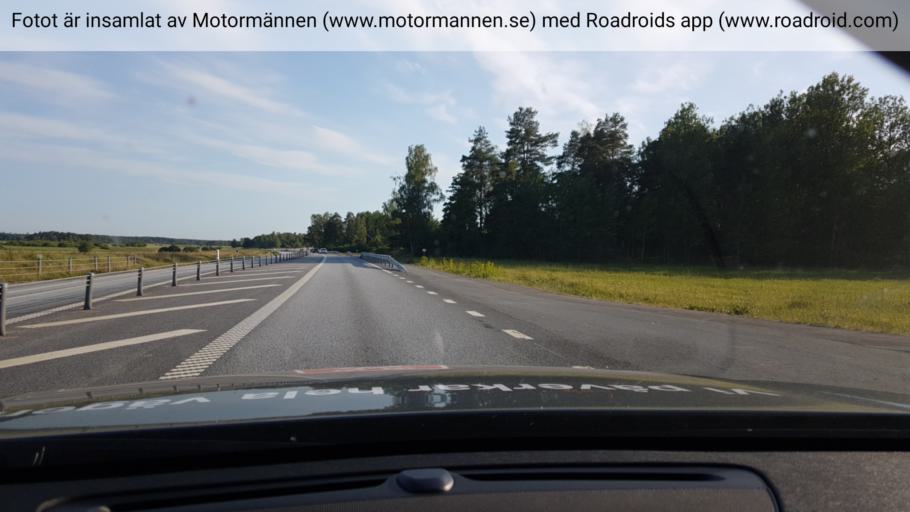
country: SE
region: Uppsala
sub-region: Osthammars Kommun
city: Gimo
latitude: 60.0472
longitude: 18.0473
